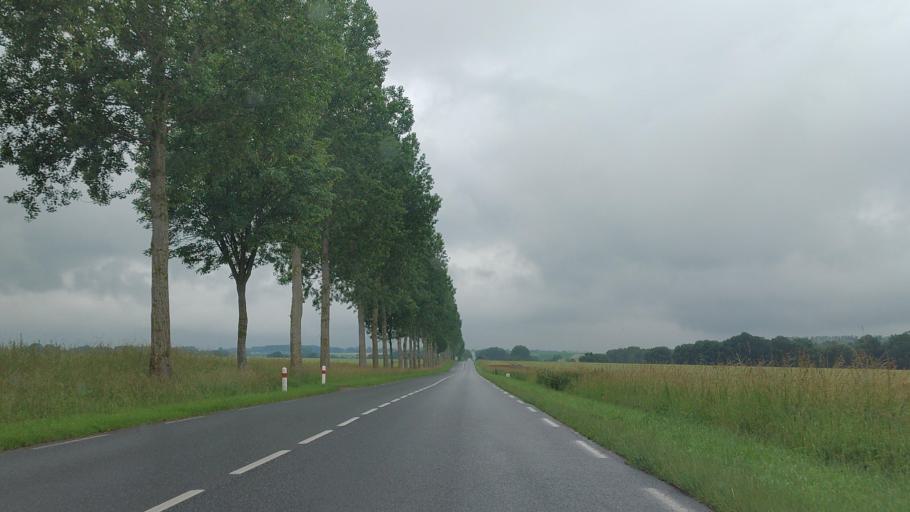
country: FR
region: Picardie
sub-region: Departement de la Somme
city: Chepy
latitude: 50.0902
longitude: 1.6904
